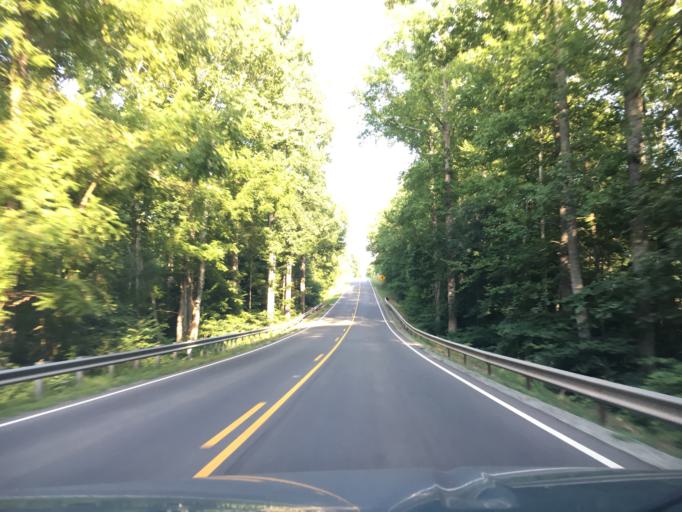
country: US
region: Virginia
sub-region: Franklin County
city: Union Hall
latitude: 36.9700
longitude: -79.5983
